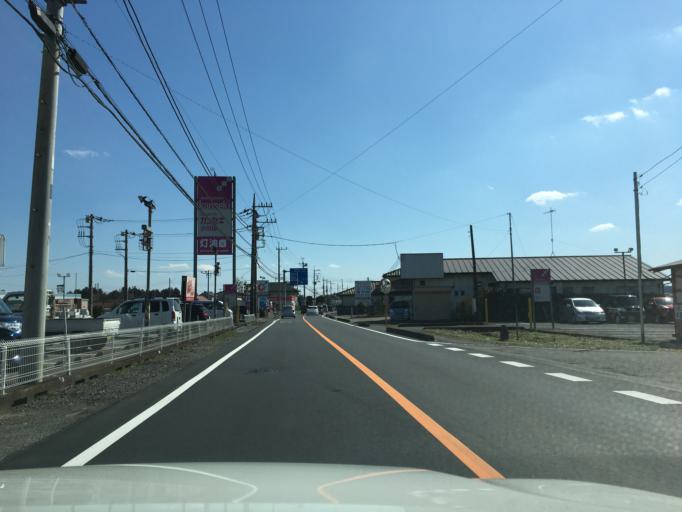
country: JP
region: Tochigi
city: Karasuyama
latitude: 36.7702
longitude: 140.1261
